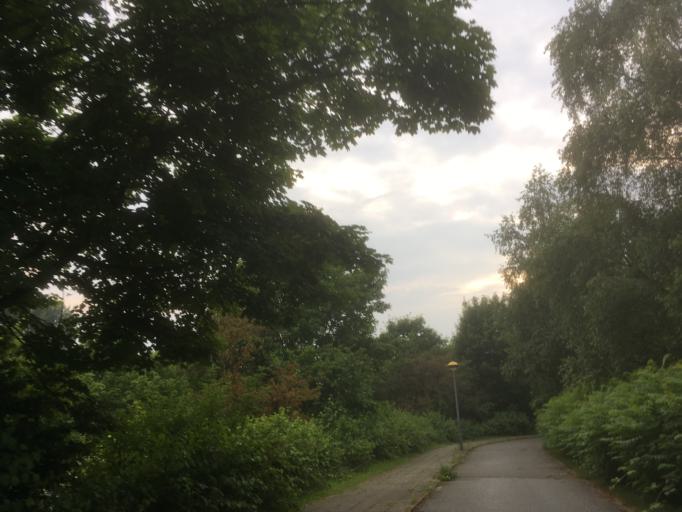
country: NL
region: Flevoland
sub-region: Gemeente Lelystad
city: Lelystad
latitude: 52.5208
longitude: 5.4672
